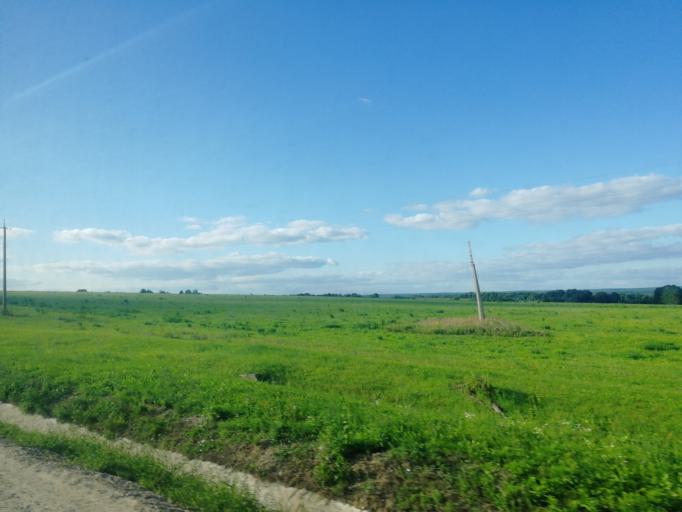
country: RU
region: Tula
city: Leninskiy
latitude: 54.2424
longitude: 37.3348
